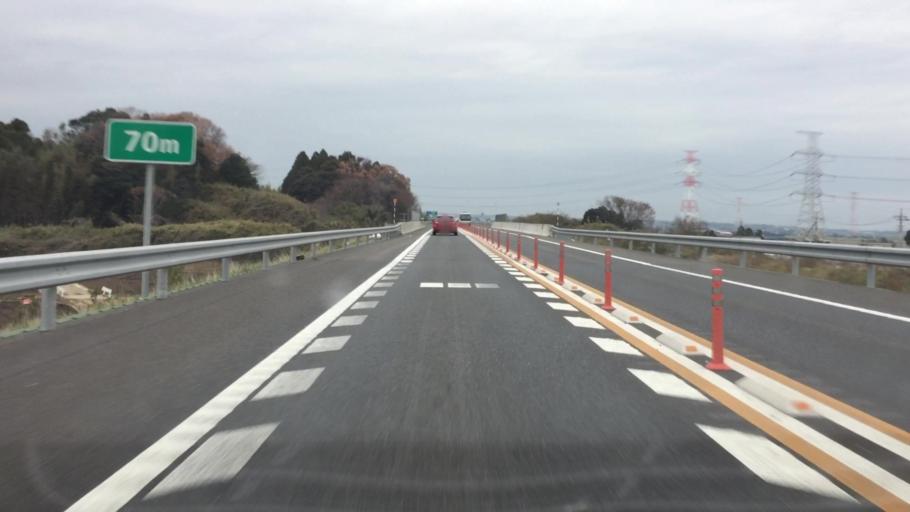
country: JP
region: Ibaraki
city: Edosaki
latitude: 35.8811
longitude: 140.3849
